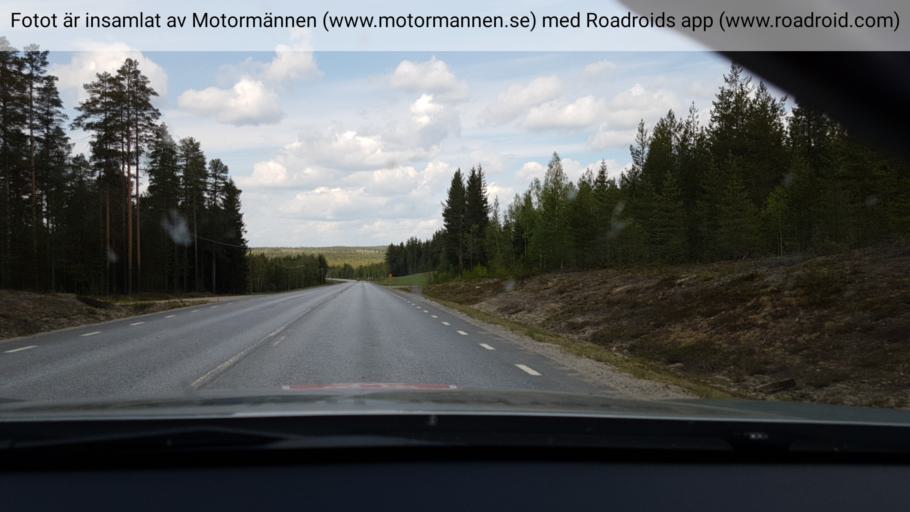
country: SE
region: Vaesterbotten
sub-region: Vannas Kommun
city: Vaennaes
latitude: 64.0335
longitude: 19.6919
